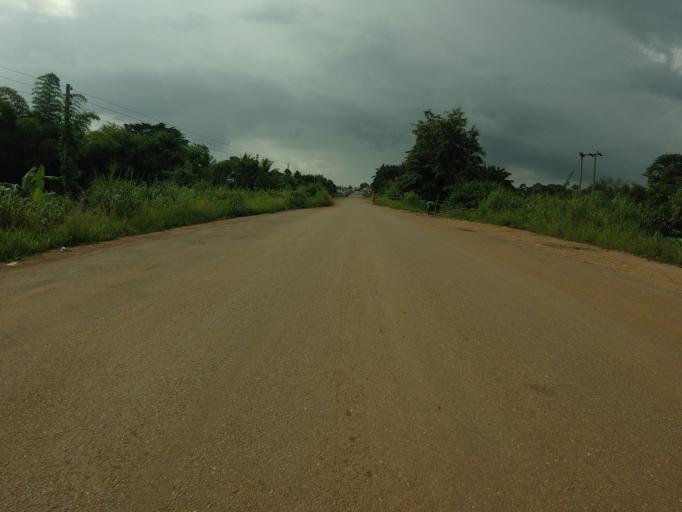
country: GH
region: Volta
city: Kpandu
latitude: 6.9935
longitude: 0.4394
